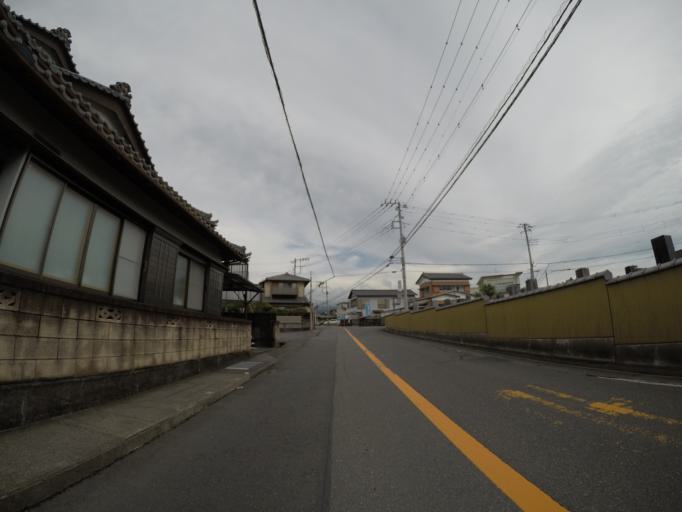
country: JP
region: Shizuoka
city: Fuji
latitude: 35.1926
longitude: 138.6519
